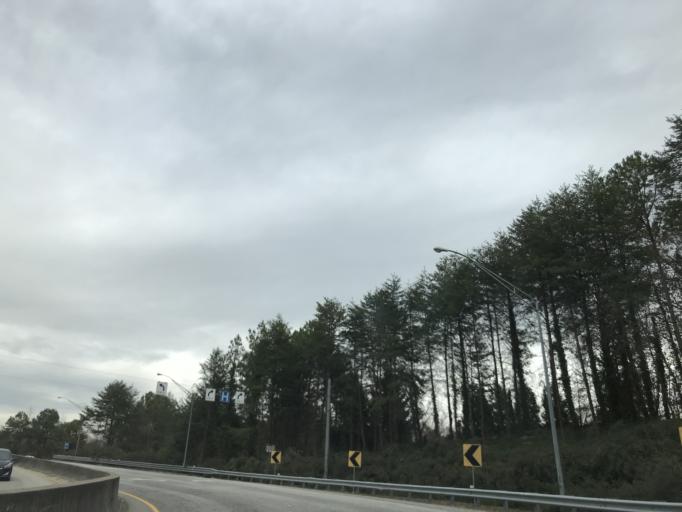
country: US
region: Georgia
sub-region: Fulton County
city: Sandy Springs
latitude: 33.9015
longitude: -84.3582
